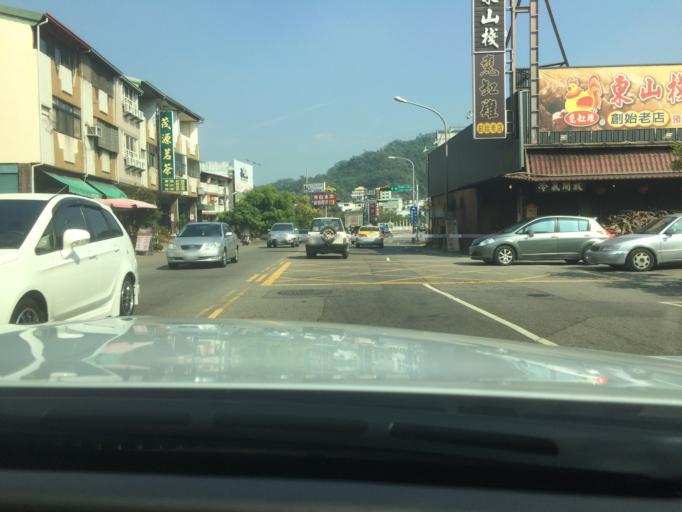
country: TW
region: Taiwan
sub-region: Taichung City
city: Taichung
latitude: 24.1782
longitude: 120.7364
